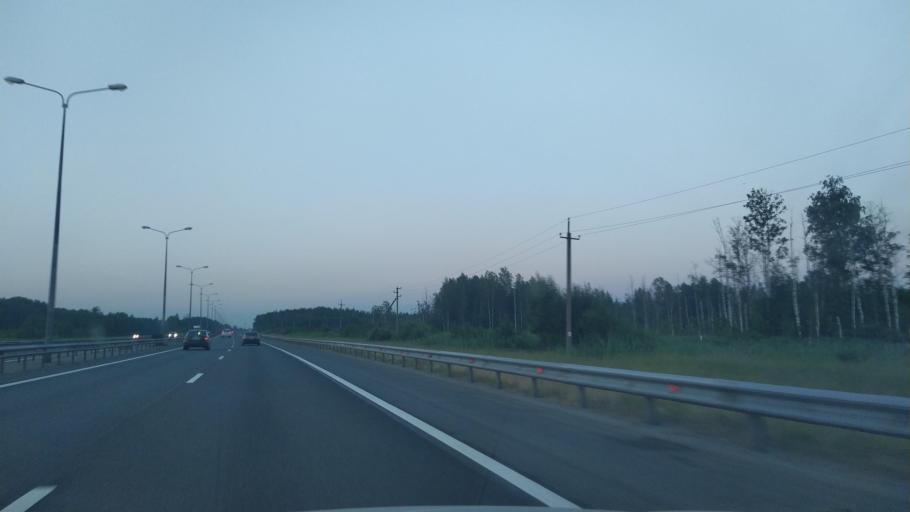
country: RU
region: St.-Petersburg
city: Lisiy Nos
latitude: 60.0400
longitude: 30.0102
